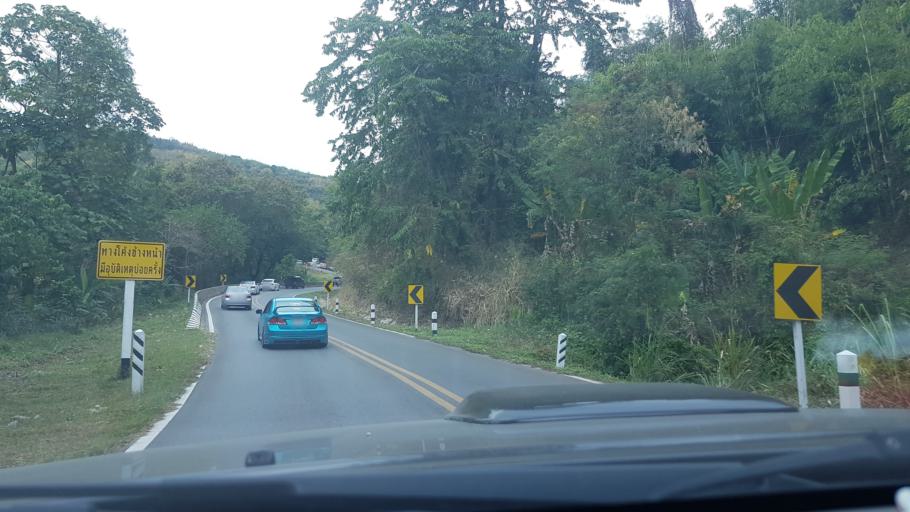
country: TH
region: Phetchabun
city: Khao Kho
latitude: 16.5446
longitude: 101.0423
